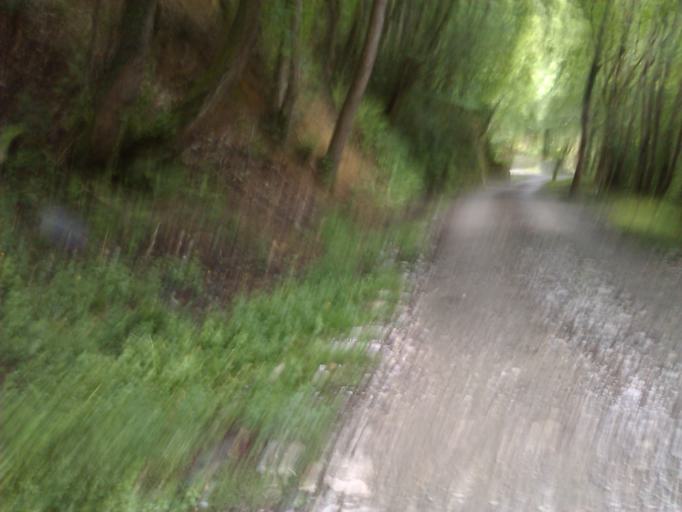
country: ES
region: Basque Country
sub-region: Provincia de Guipuzcoa
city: Berastegui
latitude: 43.1386
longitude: -1.9498
